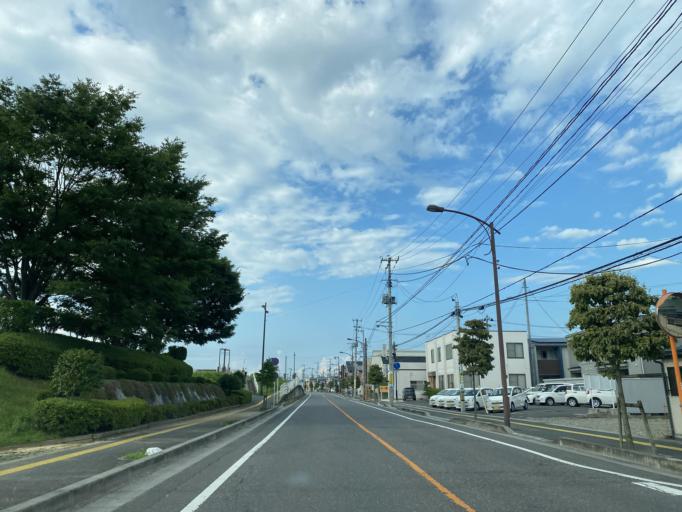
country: JP
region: Fukushima
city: Koriyama
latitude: 37.3634
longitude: 140.3835
